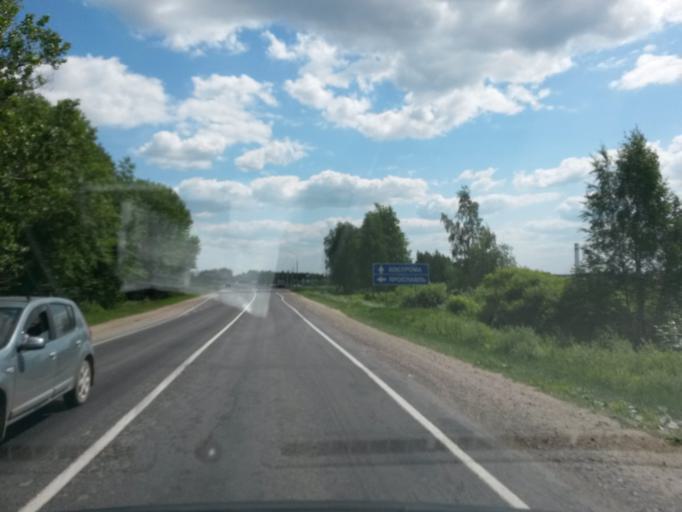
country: RU
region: Jaroslavl
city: Yaroslavl
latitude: 57.5520
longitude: 39.8849
